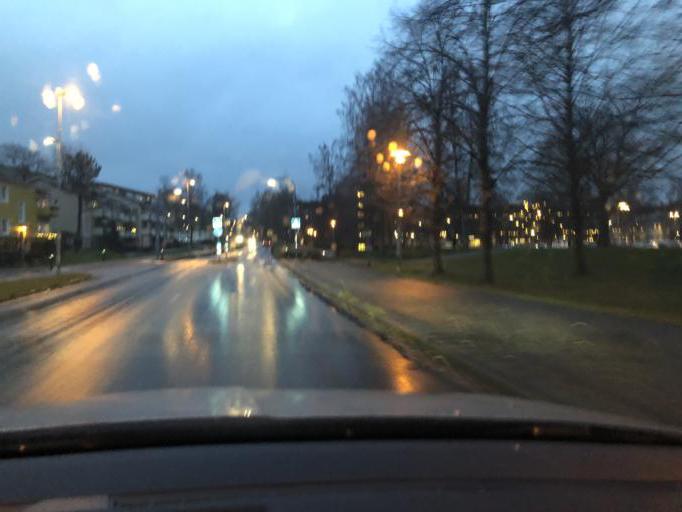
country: SE
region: Vaermland
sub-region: Karlstads Kommun
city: Karlstad
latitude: 59.3783
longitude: 13.4821
